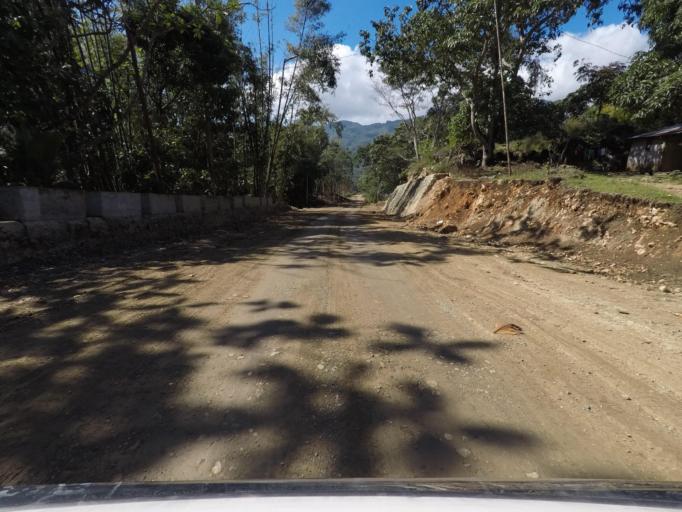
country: TL
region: Baucau
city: Venilale
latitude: -8.6599
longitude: 126.3700
